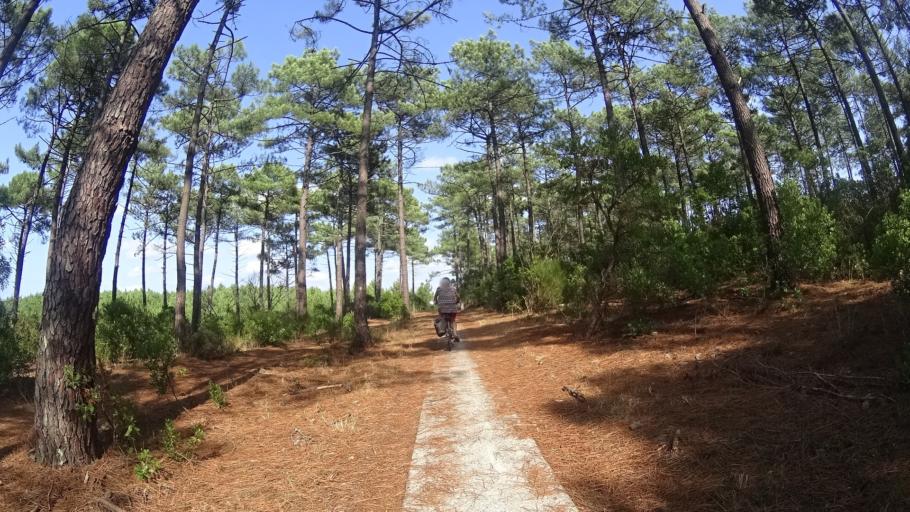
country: FR
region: Aquitaine
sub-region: Departement de la Gironde
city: Lacanau
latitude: 44.9639
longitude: -1.1909
